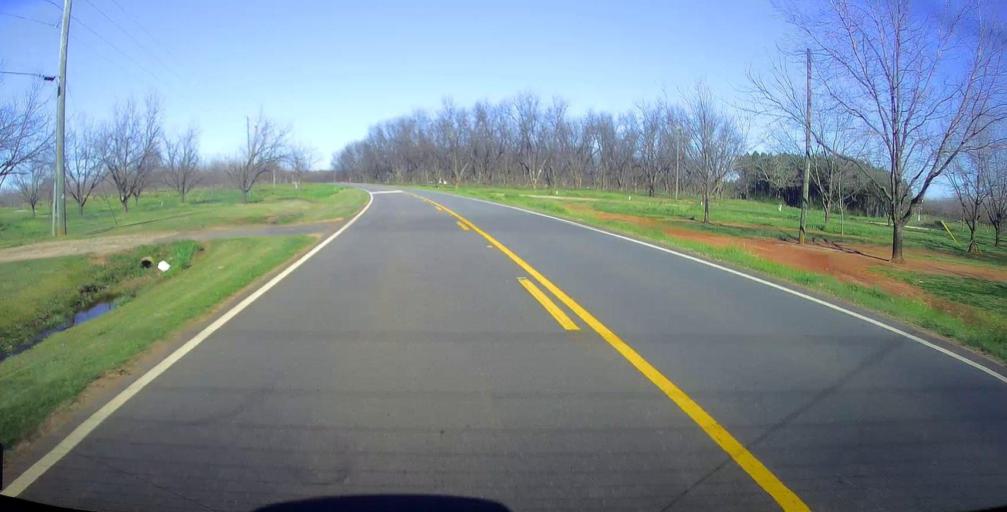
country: US
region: Georgia
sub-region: Peach County
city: Byron
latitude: 32.6751
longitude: -83.8569
